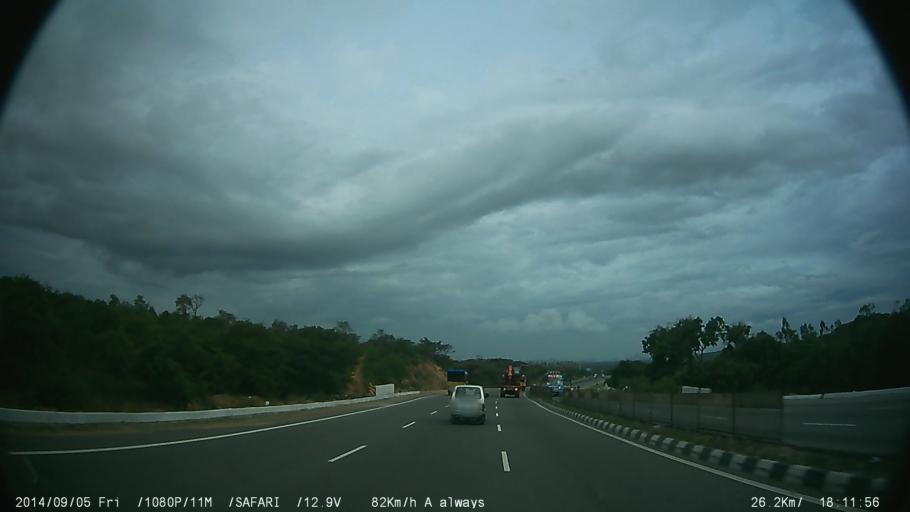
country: IN
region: Tamil Nadu
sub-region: Krishnagiri
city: Hosur
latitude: 12.6977
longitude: 77.9136
